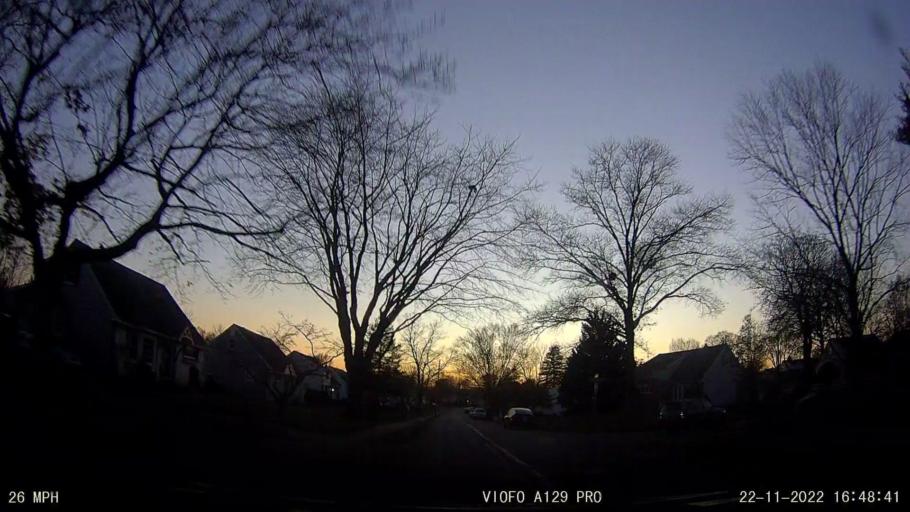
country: US
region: Pennsylvania
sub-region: Montgomery County
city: King of Prussia
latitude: 40.0990
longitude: -75.3740
